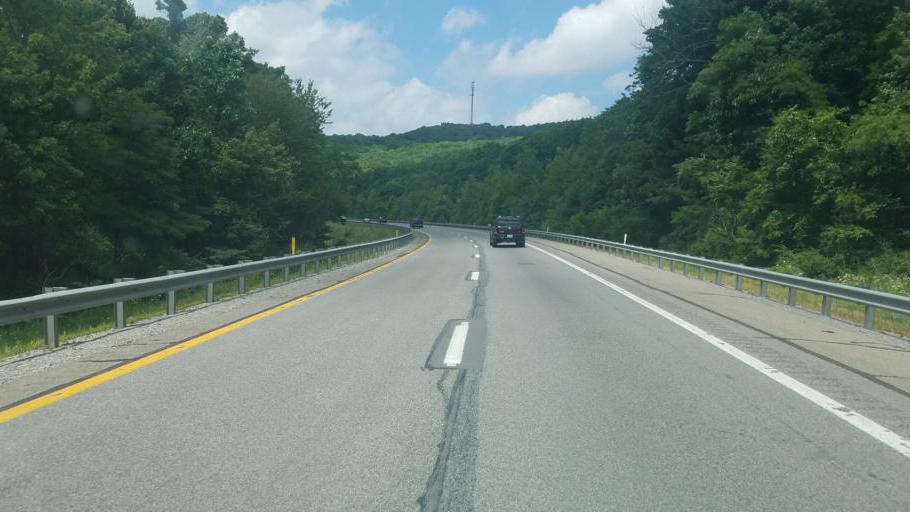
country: US
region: West Virginia
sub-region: Raleigh County
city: Shady Spring
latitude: 37.6932
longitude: -81.1281
